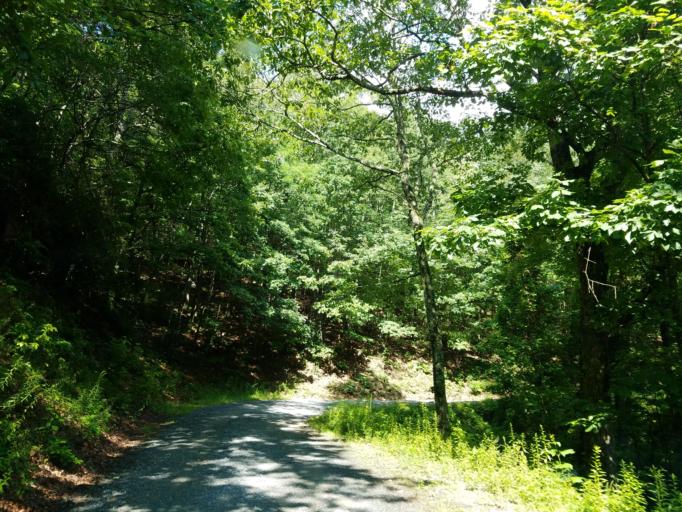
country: US
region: Georgia
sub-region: Fannin County
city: Blue Ridge
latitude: 34.6753
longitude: -84.2464
